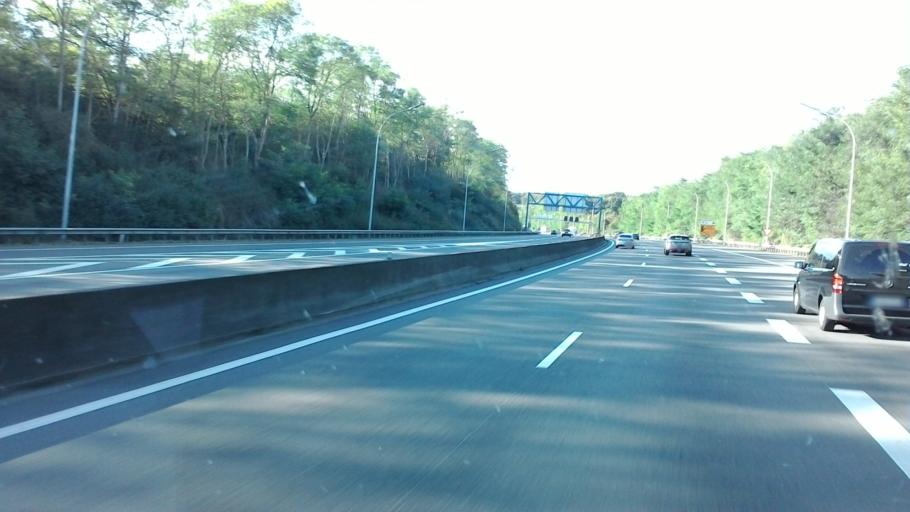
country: LU
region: Luxembourg
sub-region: Canton de Luxembourg
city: Strassen
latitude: 49.6232
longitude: 6.0819
